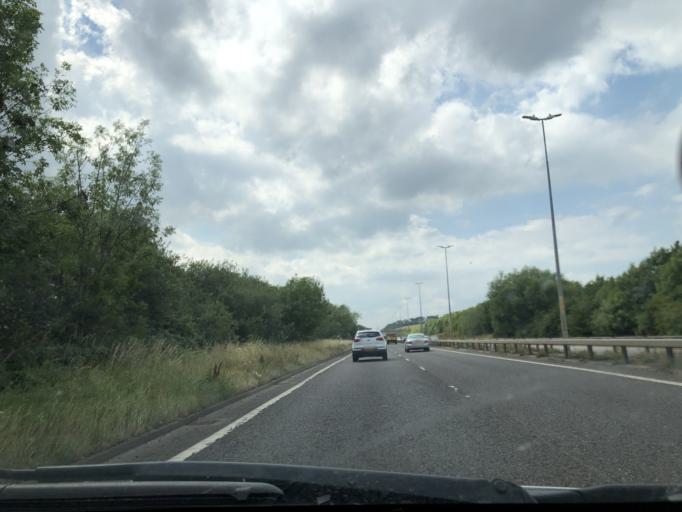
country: GB
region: England
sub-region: Kent
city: Tankerton
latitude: 51.3387
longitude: 1.0475
